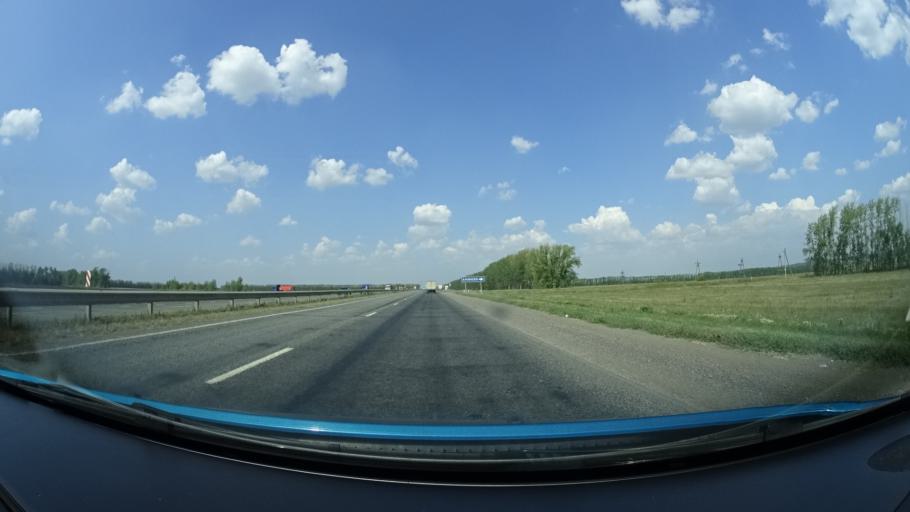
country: RU
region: Bashkortostan
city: Dmitriyevka
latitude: 54.6918
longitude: 55.2914
